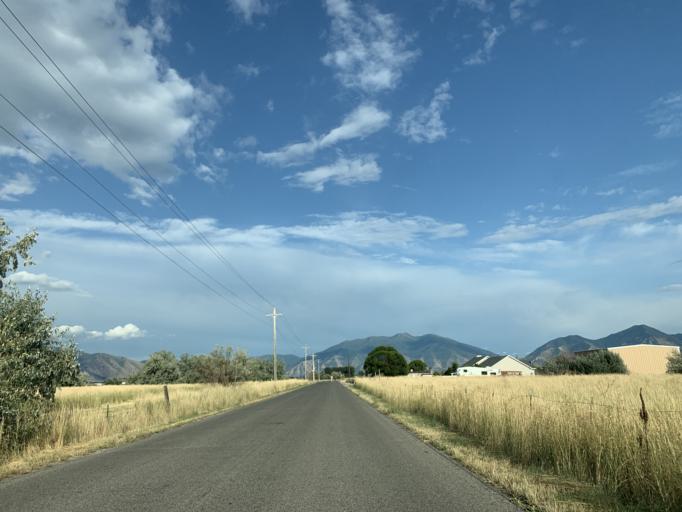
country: US
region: Utah
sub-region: Utah County
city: Benjamin
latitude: 40.1164
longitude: -111.7727
